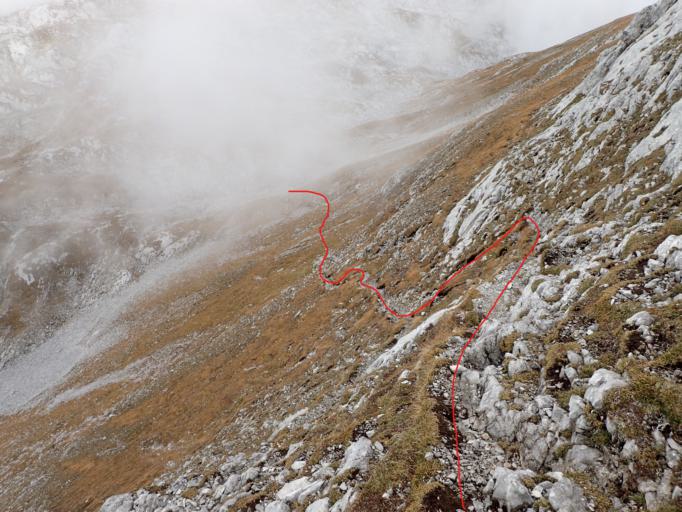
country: AT
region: Salzburg
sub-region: Politischer Bezirk Sankt Johann im Pongau
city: Werfenweng
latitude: 47.4940
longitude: 13.2435
